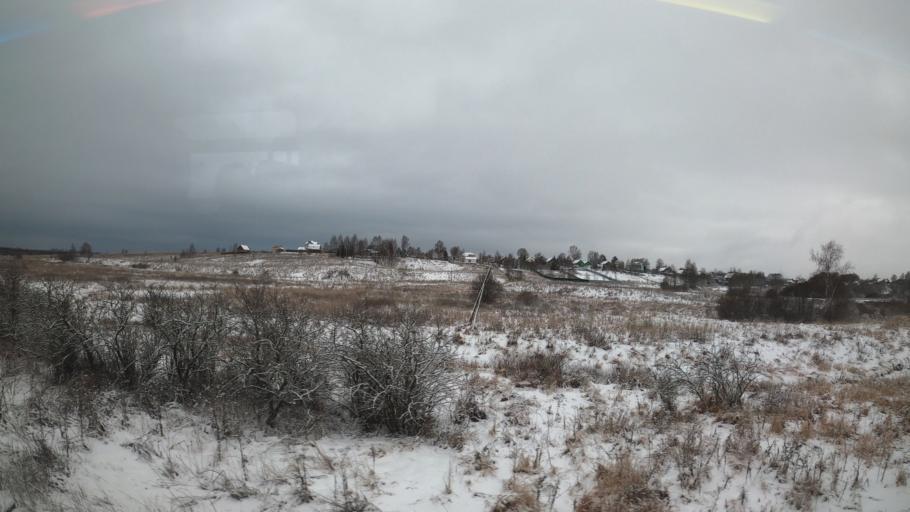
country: RU
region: Jaroslavl
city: Pereslavl'-Zalesskiy
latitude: 56.7016
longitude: 38.9122
